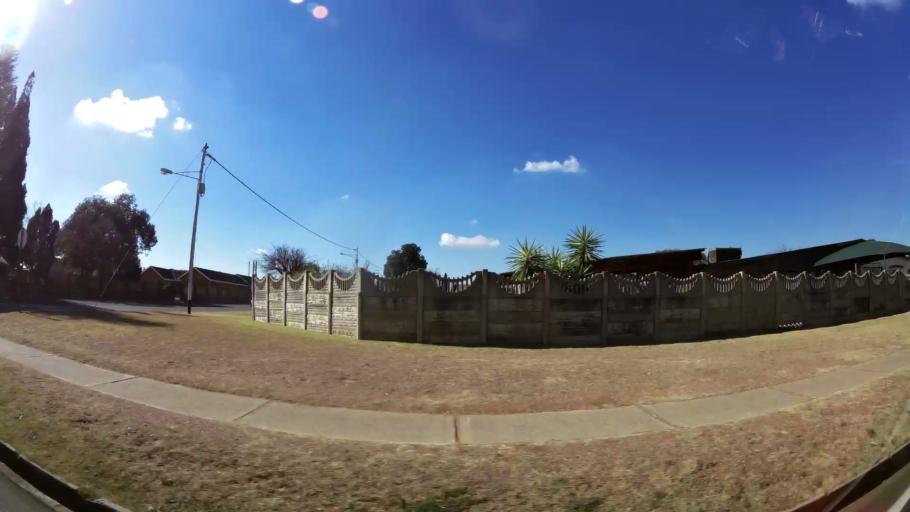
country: ZA
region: Gauteng
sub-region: City of Johannesburg Metropolitan Municipality
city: Roodepoort
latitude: -26.1424
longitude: 27.8298
